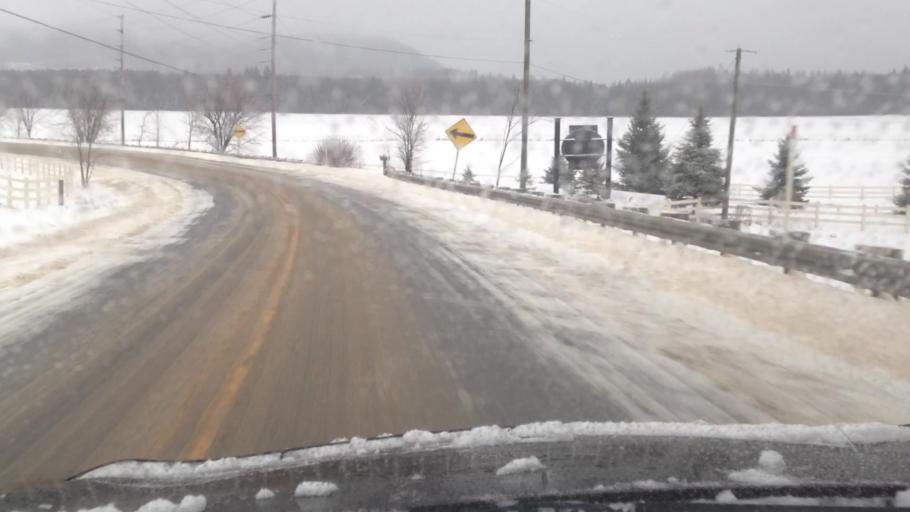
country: CA
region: Quebec
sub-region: Laurentides
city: Mont-Tremblant
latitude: 46.0379
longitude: -74.6017
